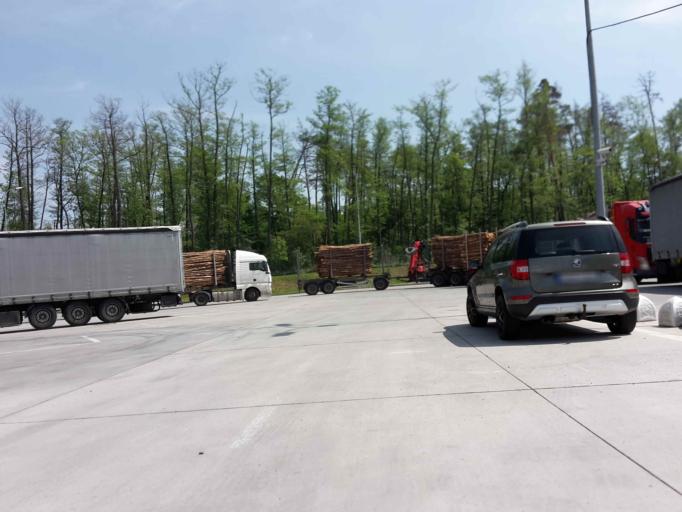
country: SK
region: Bratislavsky
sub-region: Okres Malacky
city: Malacky
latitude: 48.4170
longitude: 17.0363
